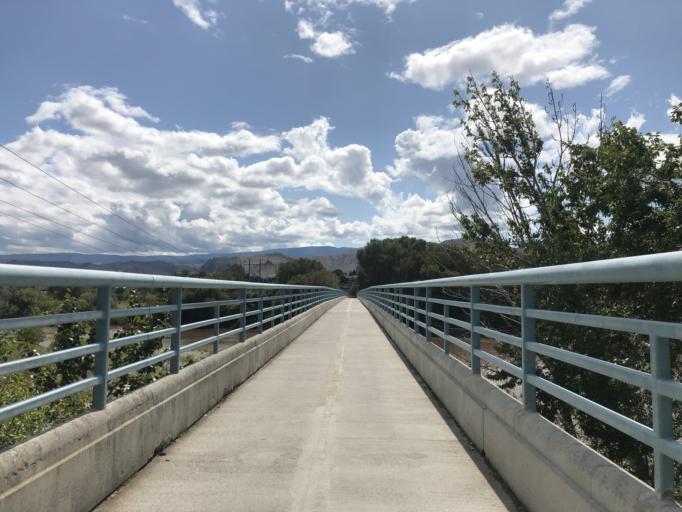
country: US
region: Washington
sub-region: Chelan County
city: Sunnyslope
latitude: 47.4586
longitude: -120.3322
